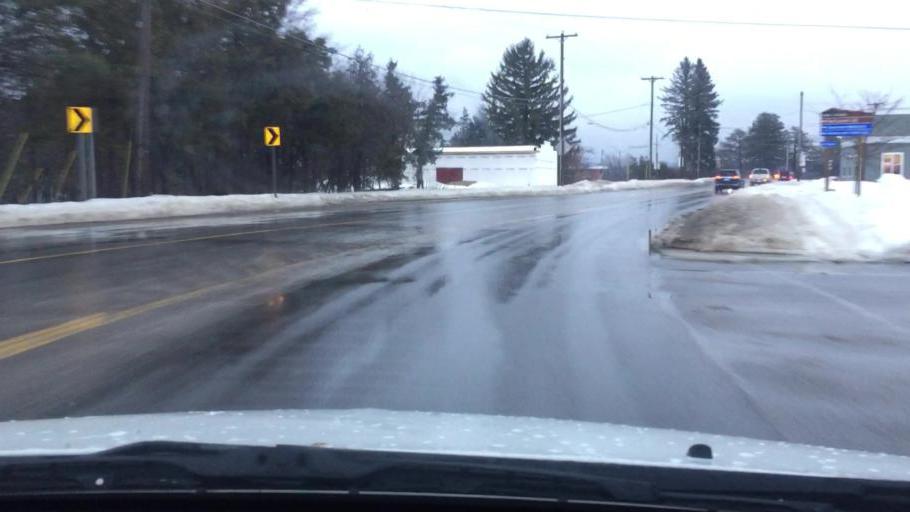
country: US
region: Michigan
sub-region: Charlevoix County
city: East Jordan
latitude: 45.1539
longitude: -85.1345
